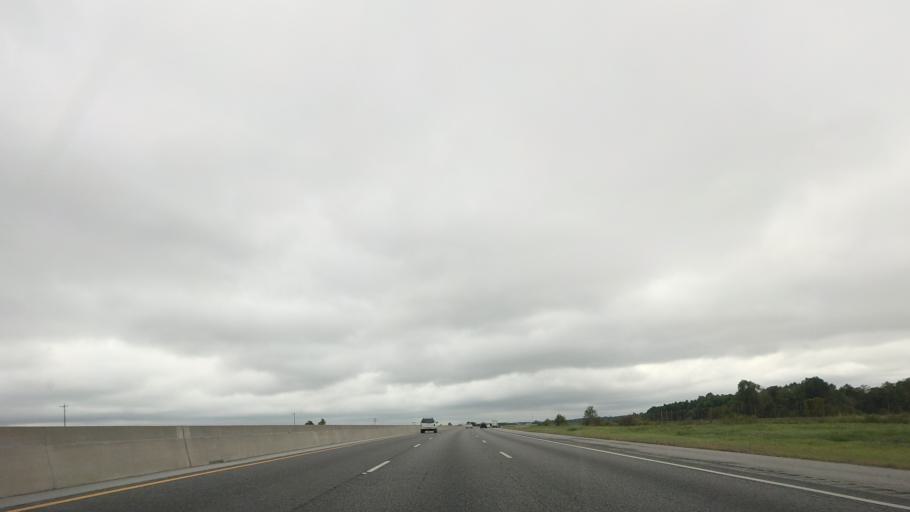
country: US
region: Georgia
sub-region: Turner County
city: Ashburn
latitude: 31.6161
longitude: -83.5682
